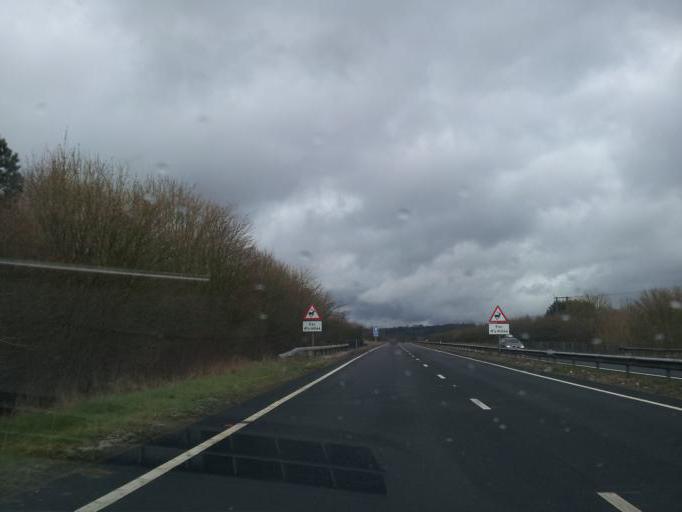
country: GB
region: England
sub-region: Somerset
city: Wincanton
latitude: 51.0589
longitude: -2.3883
